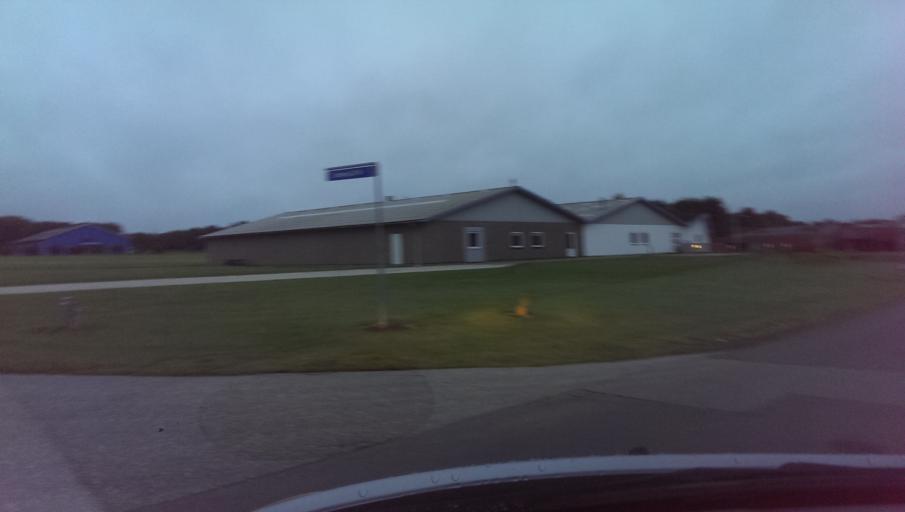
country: DK
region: South Denmark
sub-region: Varde Kommune
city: Olgod
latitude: 55.8120
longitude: 8.6366
